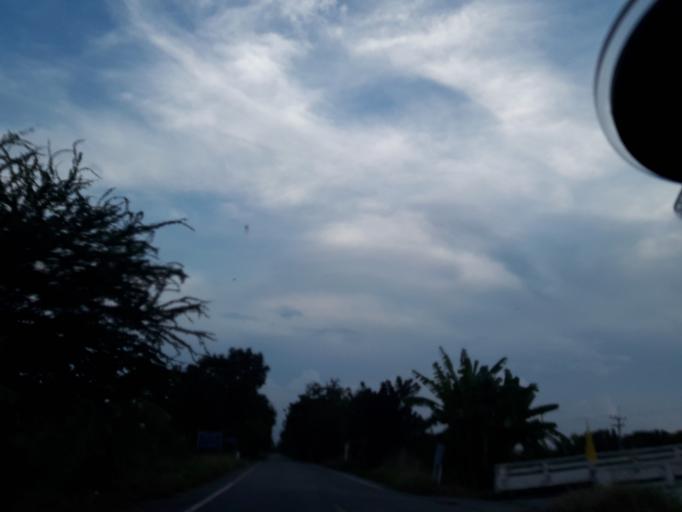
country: TH
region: Pathum Thani
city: Nong Suea
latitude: 14.1692
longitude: 100.8689
